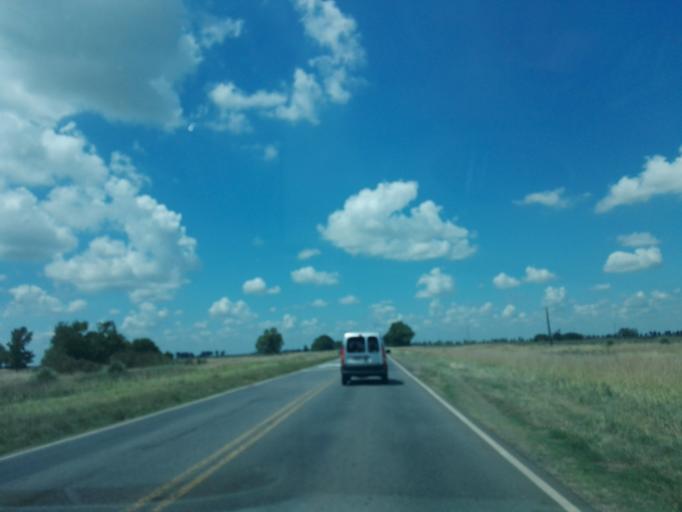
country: AR
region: Buenos Aires
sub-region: Partido de General Belgrano
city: General Belgrano
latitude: -35.8868
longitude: -58.6184
